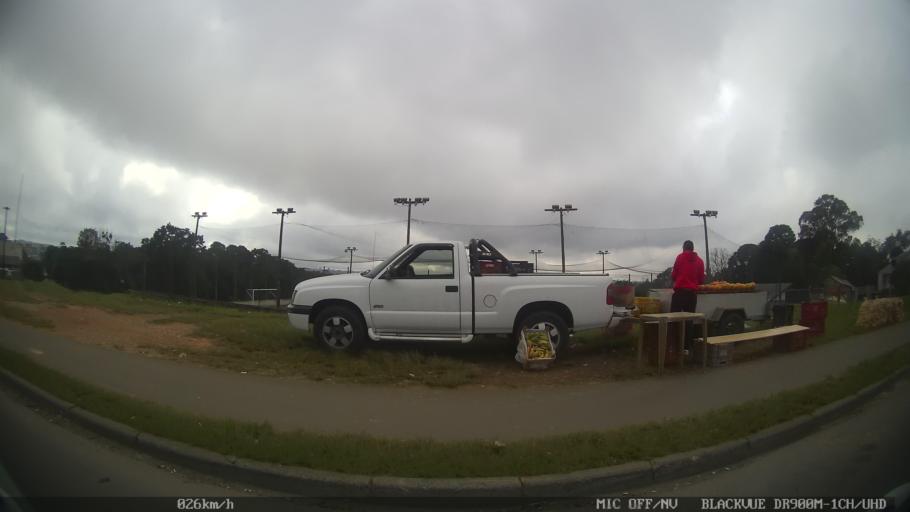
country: BR
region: Parana
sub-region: Almirante Tamandare
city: Almirante Tamandare
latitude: -25.3440
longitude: -49.2669
